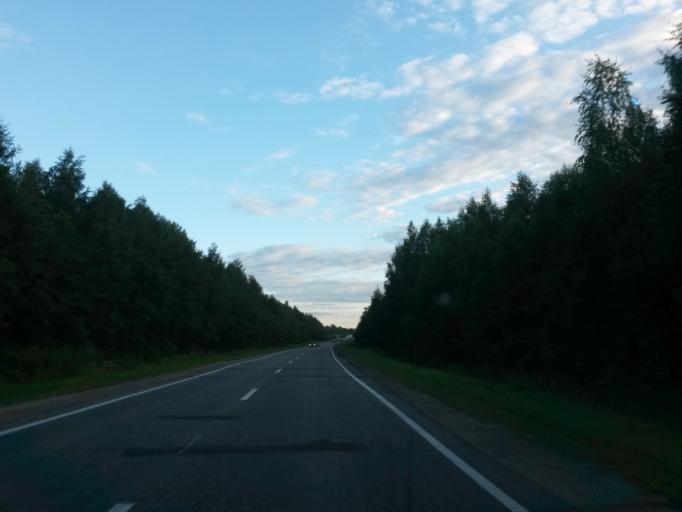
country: RU
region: Jaroslavl
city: Gavrilov-Yam
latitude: 57.3993
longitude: 39.9208
